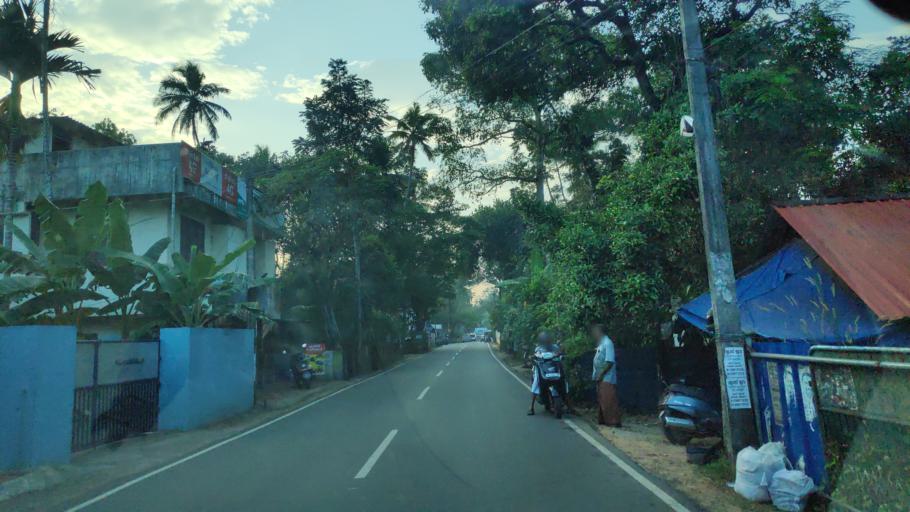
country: IN
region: Kerala
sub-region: Alappuzha
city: Shertallai
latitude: 9.6828
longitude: 76.3615
